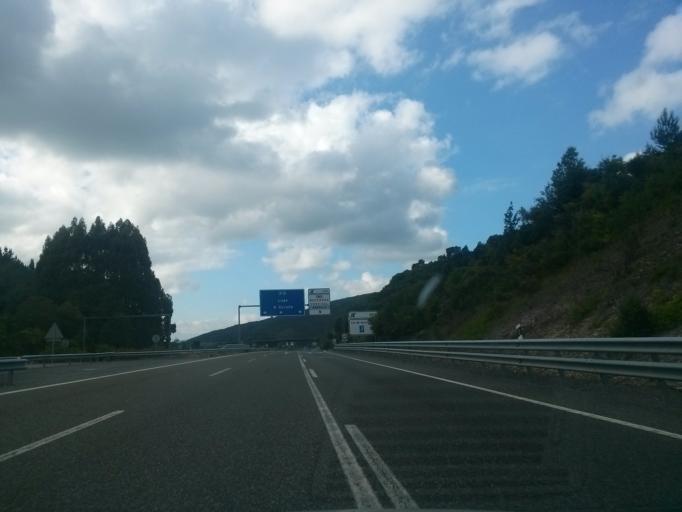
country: ES
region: Galicia
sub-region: Provincia de Lugo
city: Becerrea
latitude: 42.8750
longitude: -7.1757
